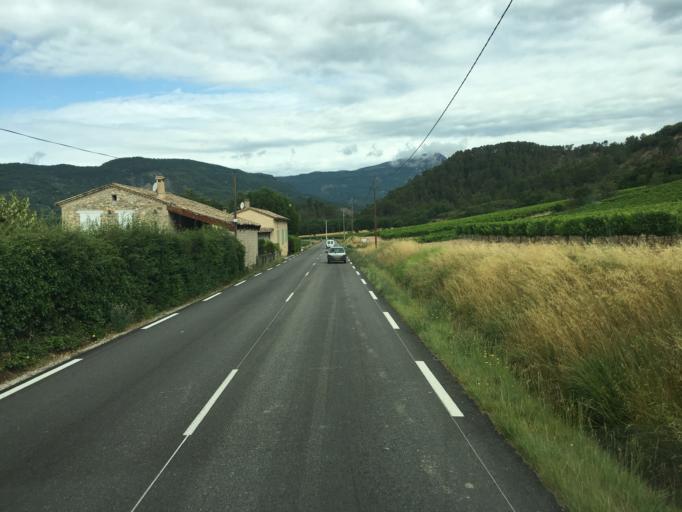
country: FR
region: Rhone-Alpes
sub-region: Departement de la Drome
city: Nyons
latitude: 44.3915
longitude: 5.2159
